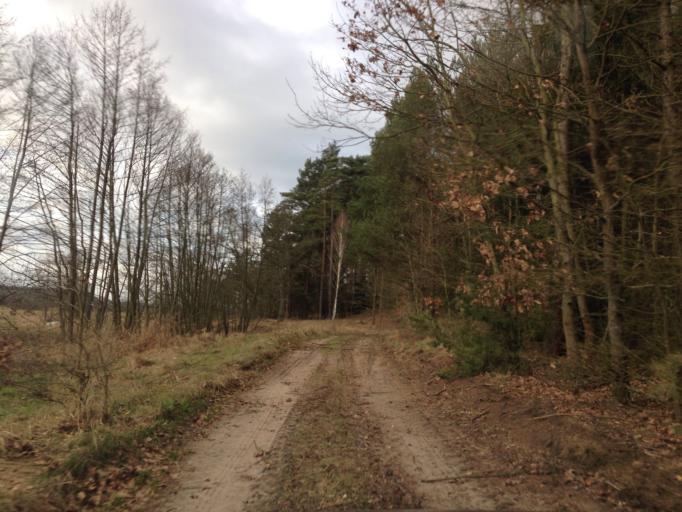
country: PL
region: Kujawsko-Pomorskie
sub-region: Powiat brodnicki
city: Gorzno
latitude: 53.2374
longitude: 19.6577
